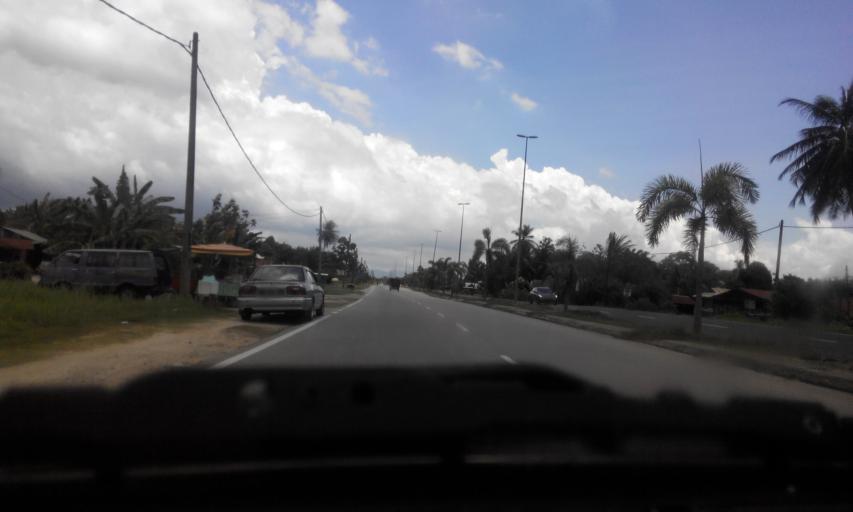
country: MY
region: Perak
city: Parit Buntar
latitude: 5.1256
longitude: 100.5142
